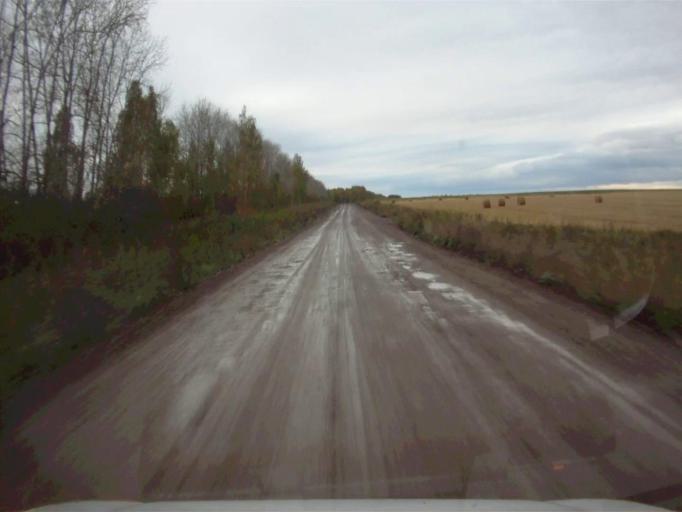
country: RU
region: Sverdlovsk
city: Mikhaylovsk
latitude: 56.1644
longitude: 59.2386
